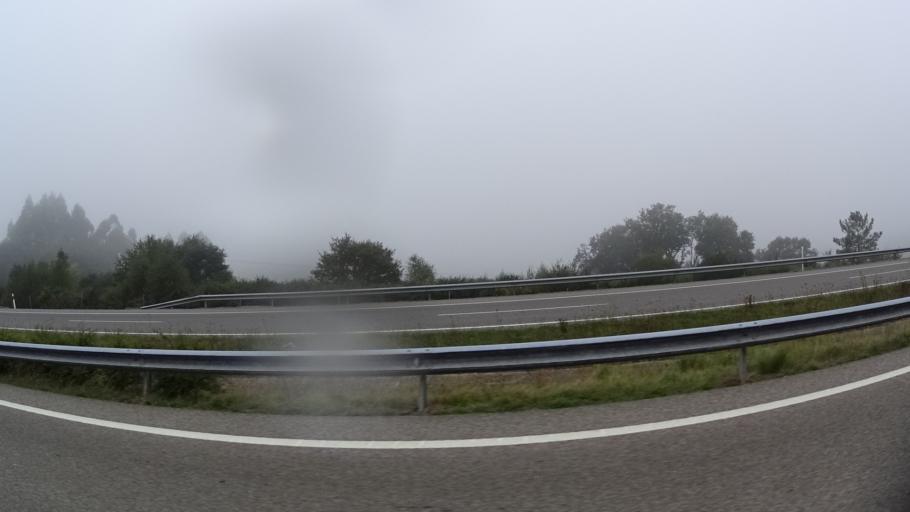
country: ES
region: Galicia
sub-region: Provincia de Lugo
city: Guitiriz
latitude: 43.1750
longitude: -7.7978
